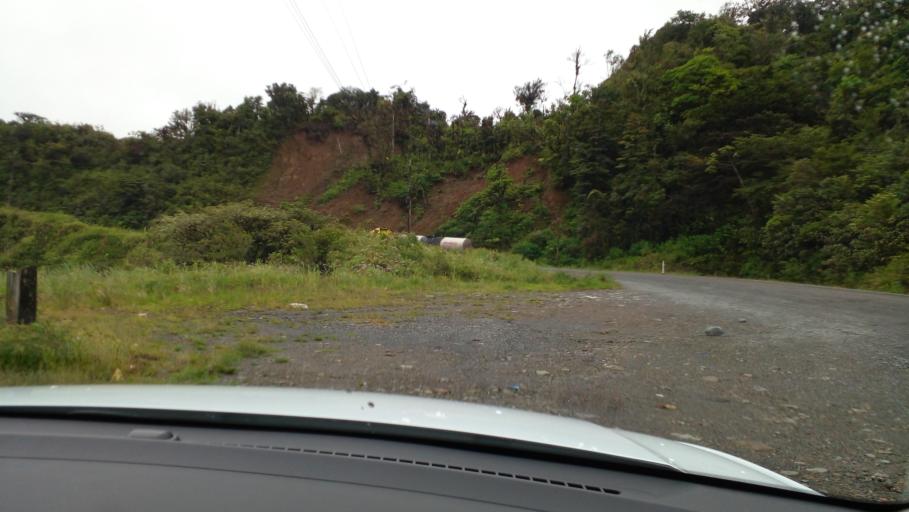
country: PA
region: Chiriqui
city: Gualaca
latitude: 8.6879
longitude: -82.2283
